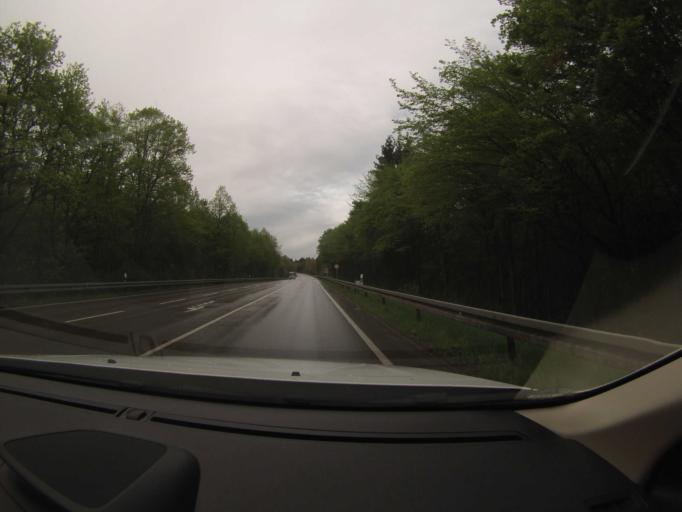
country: DE
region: Bavaria
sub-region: Upper Bavaria
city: Taufkirchen
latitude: 48.0273
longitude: 11.6355
